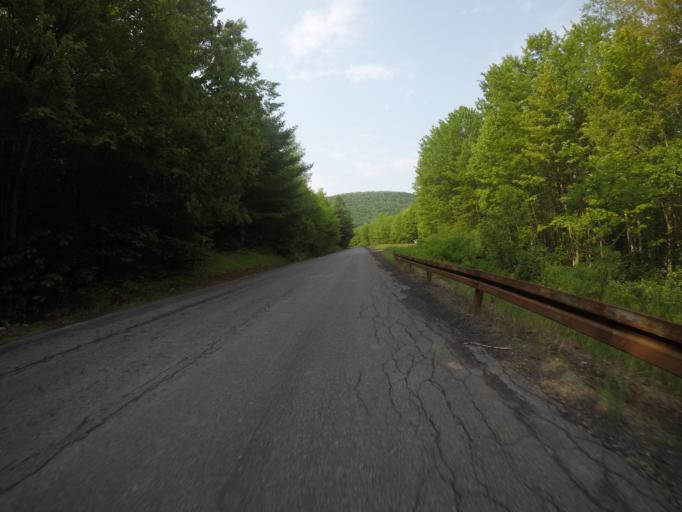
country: US
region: New York
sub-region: Sullivan County
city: Livingston Manor
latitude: 42.0898
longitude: -74.7920
